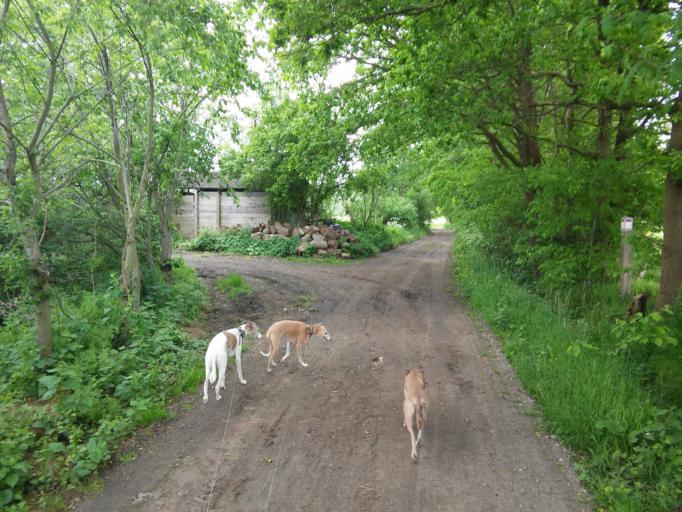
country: BE
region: Flanders
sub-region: Provincie Antwerpen
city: Mechelen
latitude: 51.0299
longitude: 4.4396
